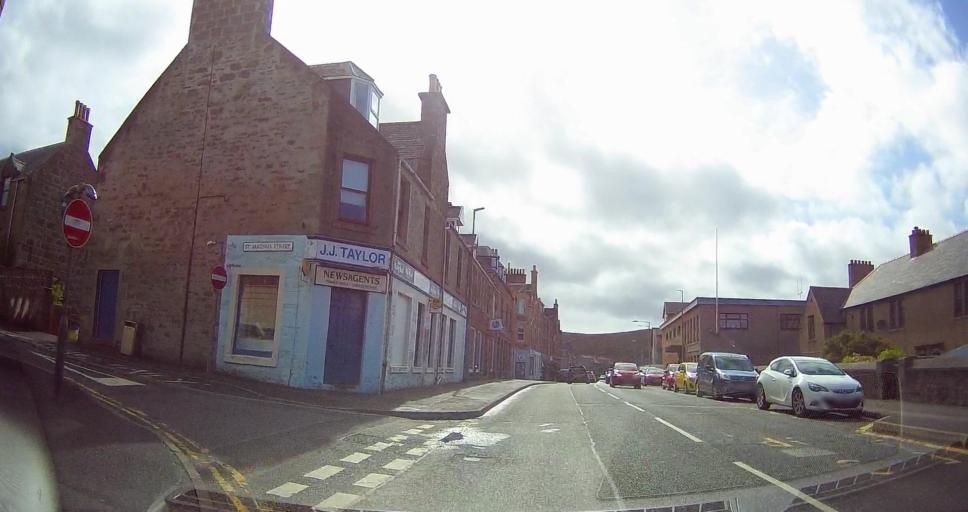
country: GB
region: Scotland
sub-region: Shetland Islands
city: Shetland
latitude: 60.1573
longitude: -1.1480
